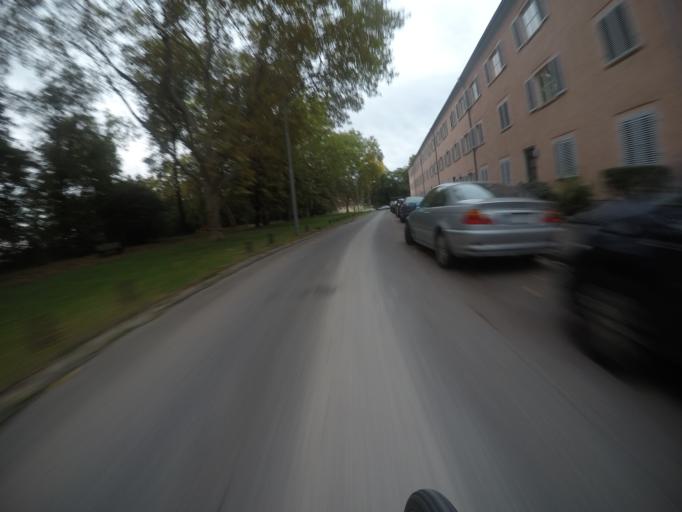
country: DE
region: Baden-Wuerttemberg
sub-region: Regierungsbezirk Stuttgart
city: Stuttgart-Ost
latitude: 48.7902
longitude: 9.2142
